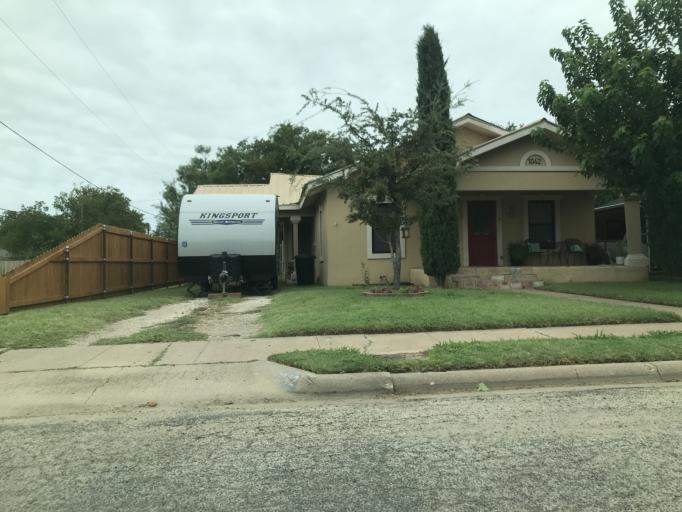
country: US
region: Texas
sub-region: Taylor County
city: Abilene
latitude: 32.4376
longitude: -99.7360
